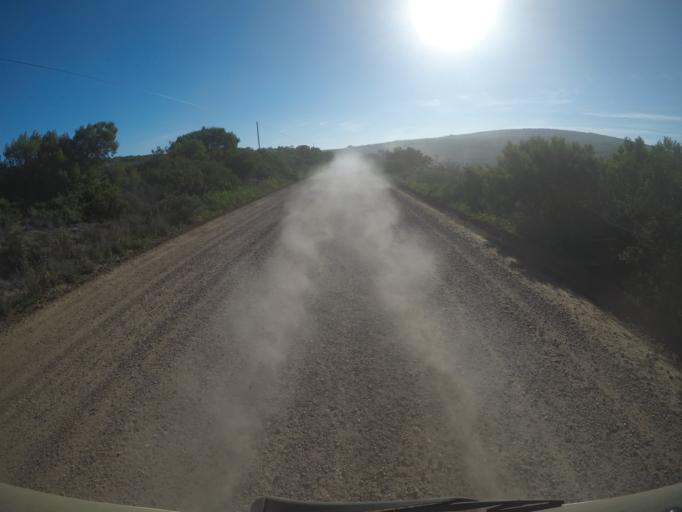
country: ZA
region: Western Cape
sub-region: Eden District Municipality
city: Mossel Bay
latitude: -34.1447
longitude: 22.0129
